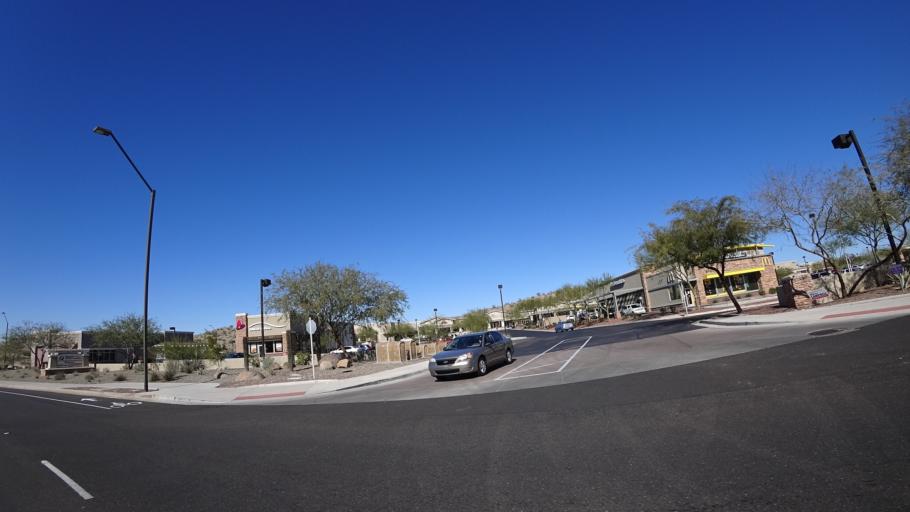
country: US
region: Arizona
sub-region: Maricopa County
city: Goodyear
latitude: 33.3560
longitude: -112.4291
